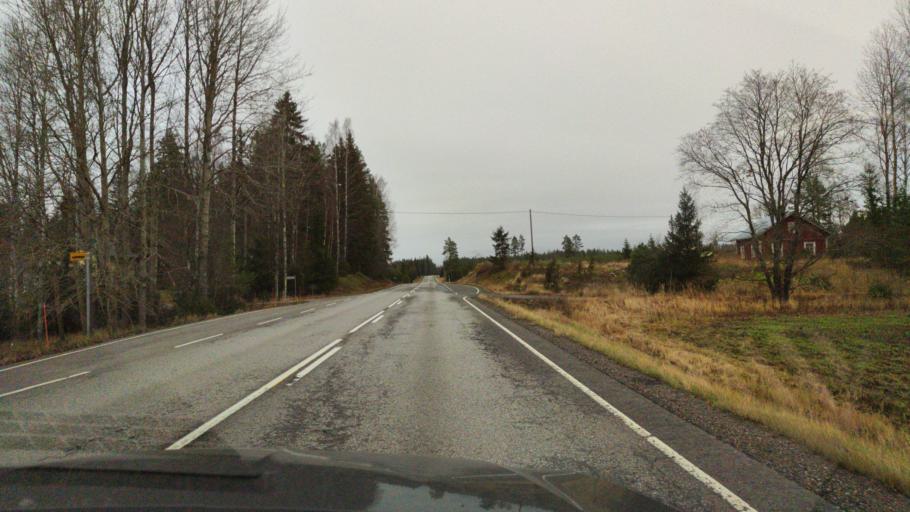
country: FI
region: Varsinais-Suomi
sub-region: Loimaa
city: Ylaene
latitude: 60.7575
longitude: 22.4298
